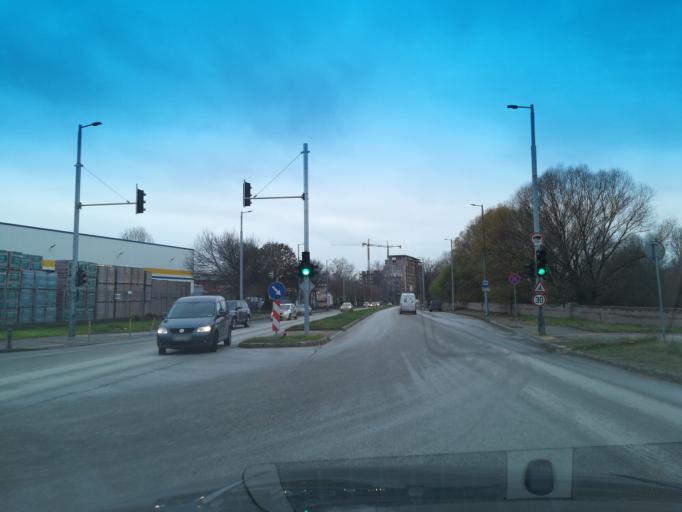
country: BG
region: Plovdiv
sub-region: Obshtina Plovdiv
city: Plovdiv
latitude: 42.1549
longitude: 24.7702
